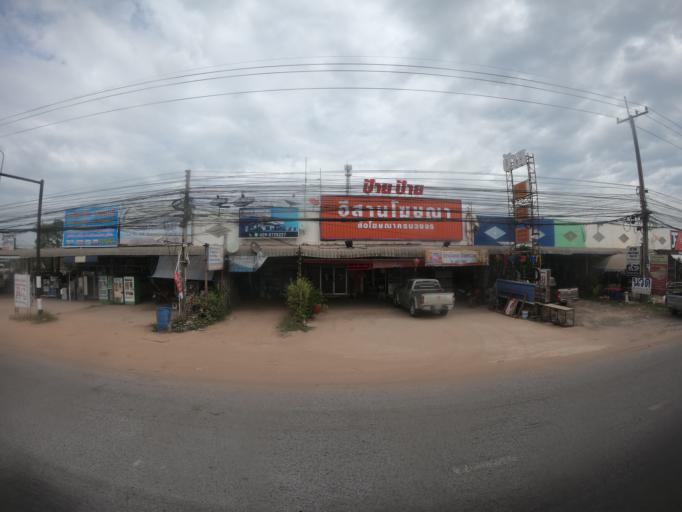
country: TH
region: Maha Sarakham
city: Maha Sarakham
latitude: 16.2147
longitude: 103.2792
